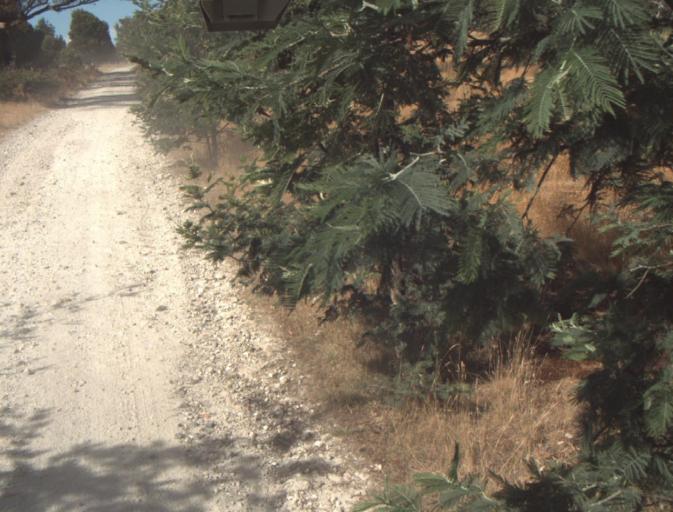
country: AU
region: Tasmania
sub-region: Dorset
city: Bridport
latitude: -41.1559
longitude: 147.2047
